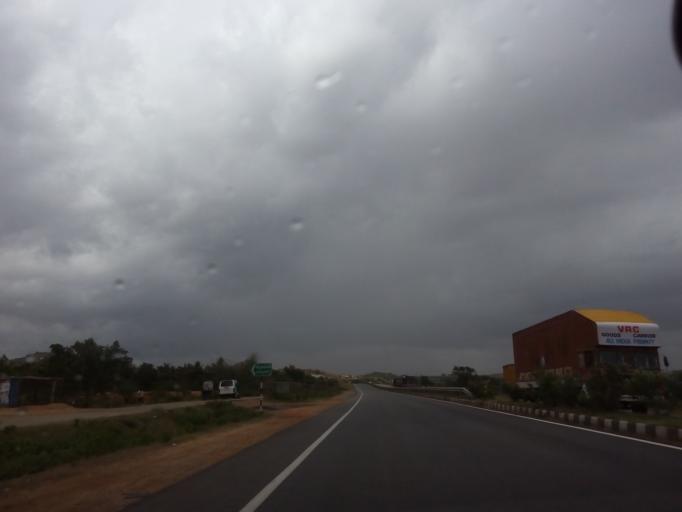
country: IN
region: Karnataka
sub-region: Chitradurga
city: Chitradurga
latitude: 14.2665
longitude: 76.3365
